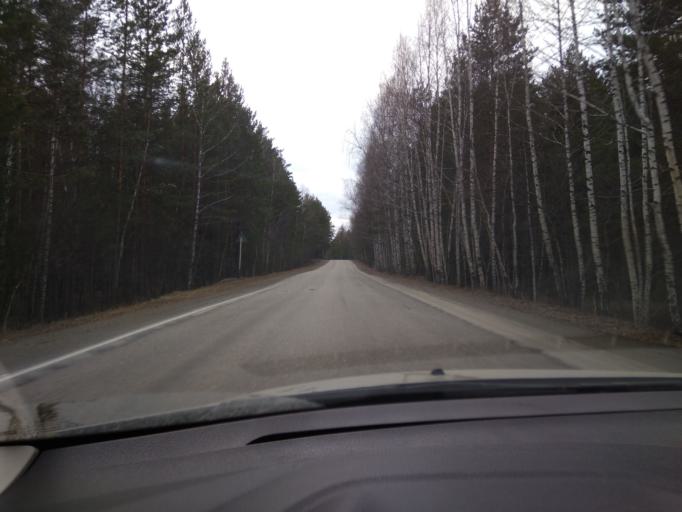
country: RU
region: Chelyabinsk
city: Kyshtym
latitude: 55.7142
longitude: 60.6136
